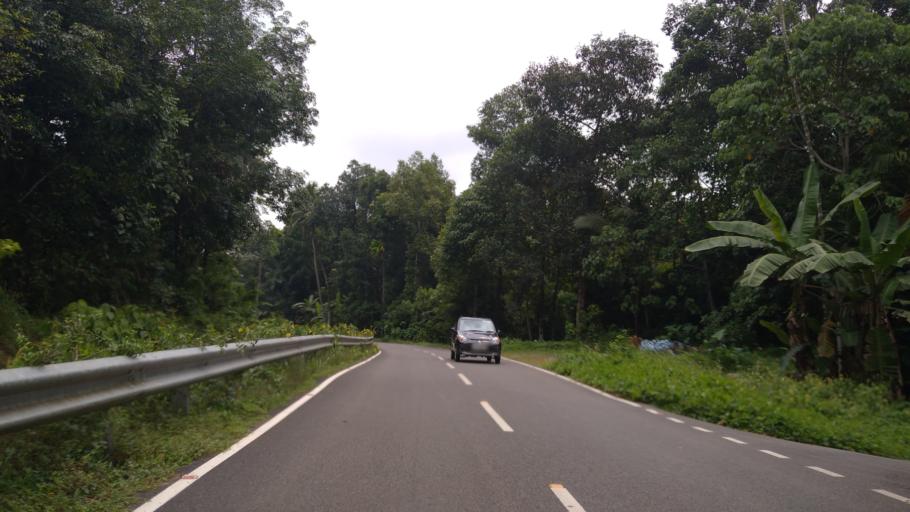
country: IN
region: Kerala
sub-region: Ernakulam
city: Ramamangalam
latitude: 10.0141
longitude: 76.4852
